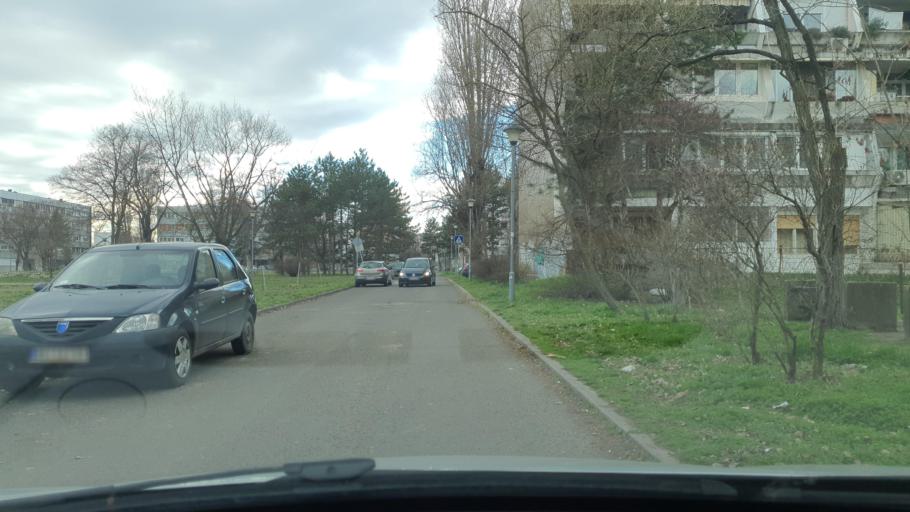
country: RS
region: Central Serbia
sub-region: Belgrade
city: Cukarica
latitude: 44.7986
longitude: 20.3931
